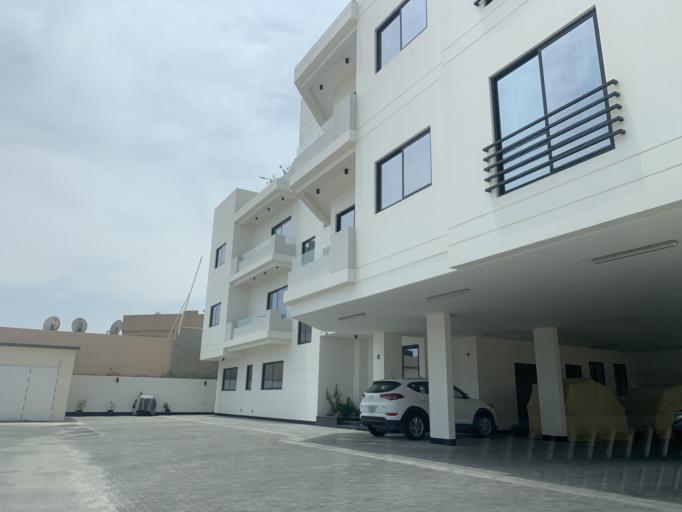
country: BH
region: Central Governorate
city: Madinat Hamad
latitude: 26.1800
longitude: 50.4759
